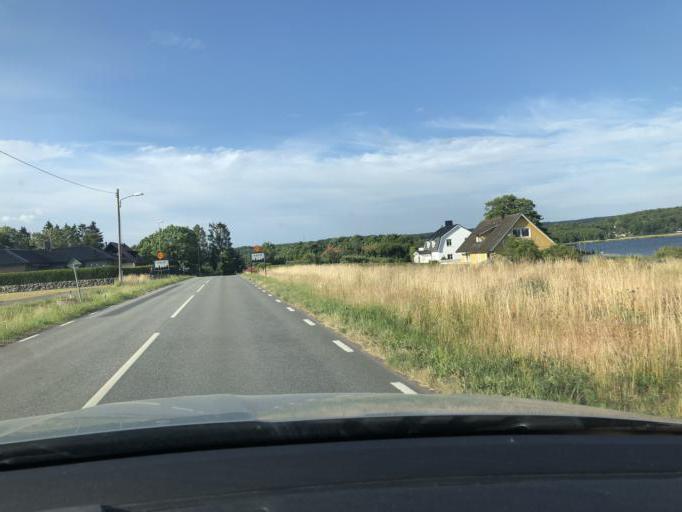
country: SE
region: Blekinge
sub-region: Solvesborgs Kommun
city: Soelvesborg
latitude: 56.0568
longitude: 14.5336
